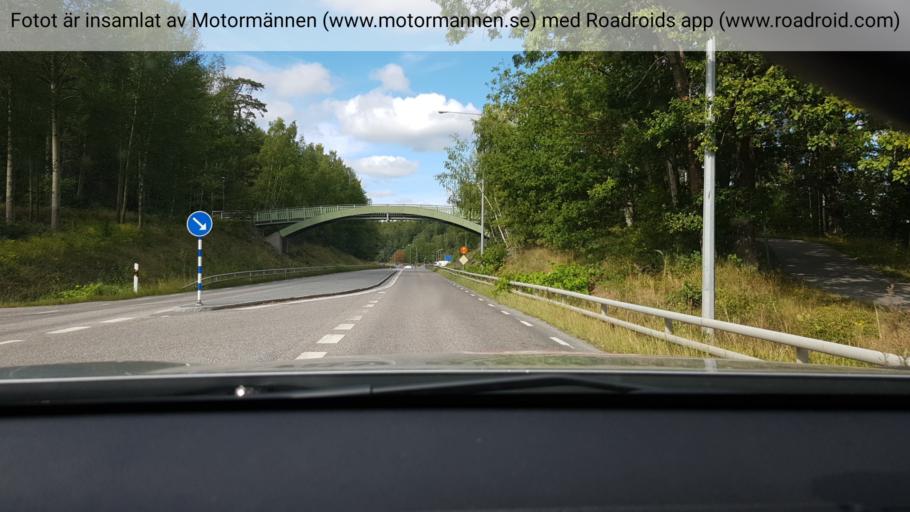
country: SE
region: Stockholm
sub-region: Vaxholms Kommun
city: Resaro
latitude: 59.4148
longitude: 18.3138
